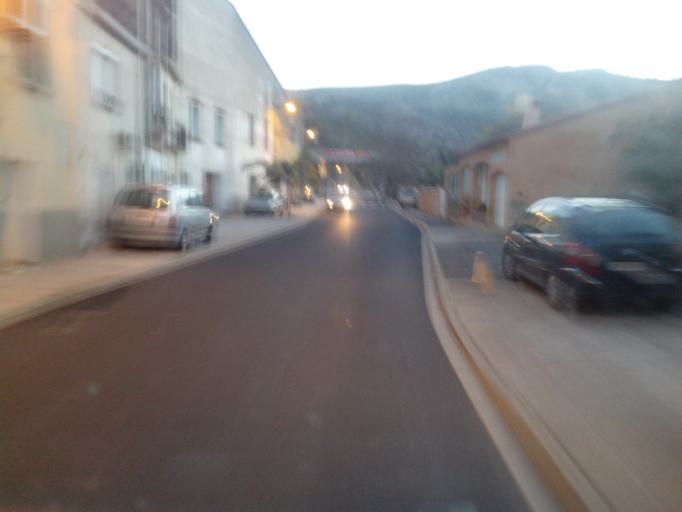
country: FR
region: Languedoc-Roussillon
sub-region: Departement des Pyrenees-Orientales
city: Baixas
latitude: 42.7775
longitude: 2.7891
